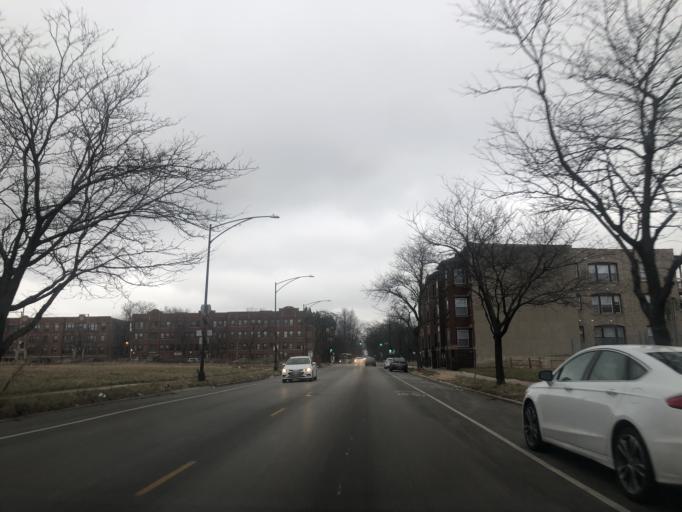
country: US
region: Illinois
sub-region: Cook County
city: Chicago
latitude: 41.7843
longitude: -87.6157
